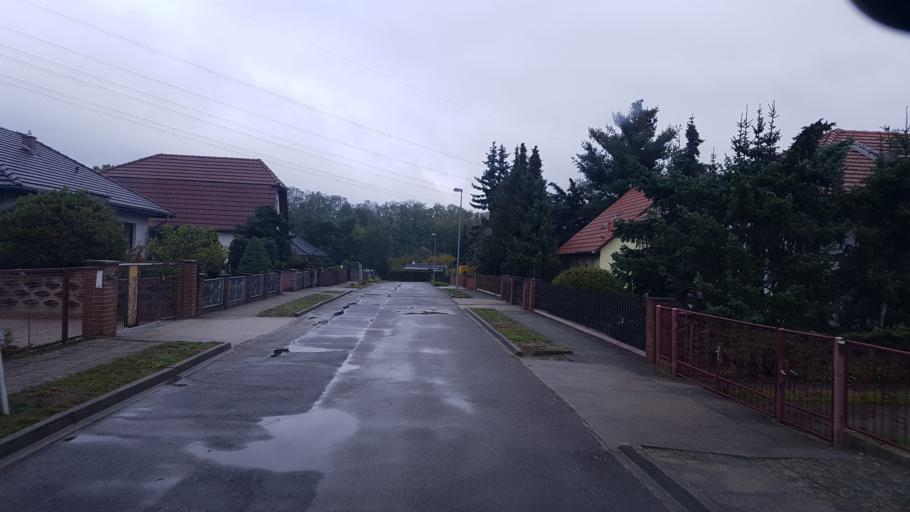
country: DE
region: Brandenburg
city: Altdobern
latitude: 51.6505
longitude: 14.0140
